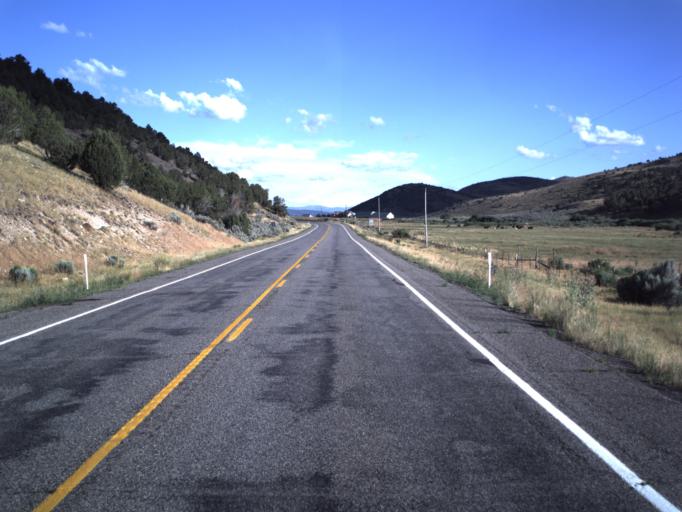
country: US
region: Utah
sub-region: Utah County
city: Woodland Hills
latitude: 39.8834
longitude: -111.5455
